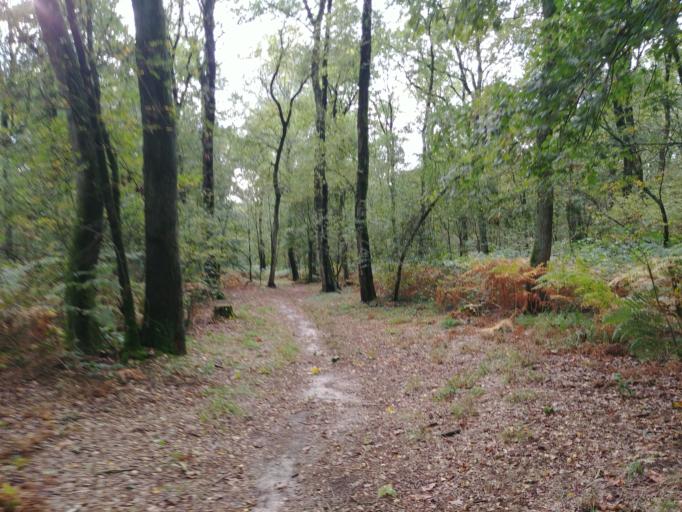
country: NL
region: Gelderland
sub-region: Gemeente Renkum
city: Doorwerth
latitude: 51.9785
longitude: 5.7892
